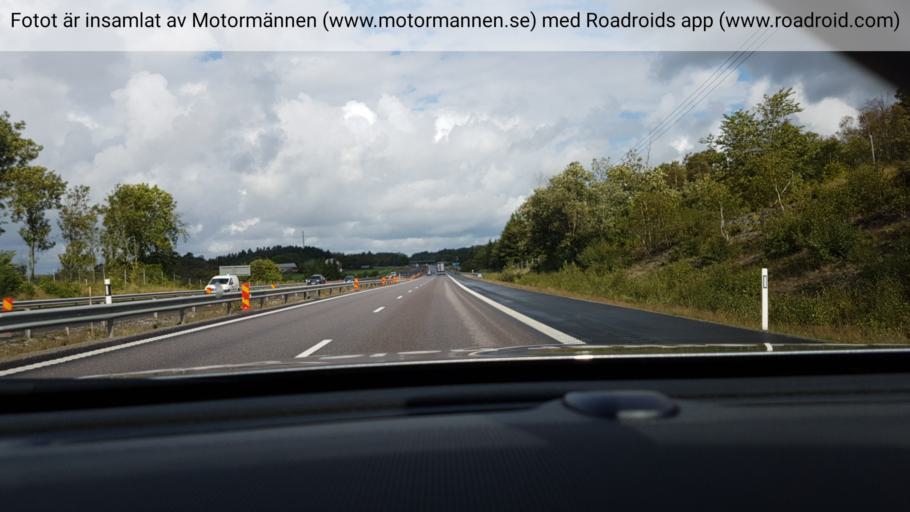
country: SE
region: Vaestra Goetaland
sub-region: Stenungsunds Kommun
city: Stora Hoga
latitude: 57.9753
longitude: 11.8401
